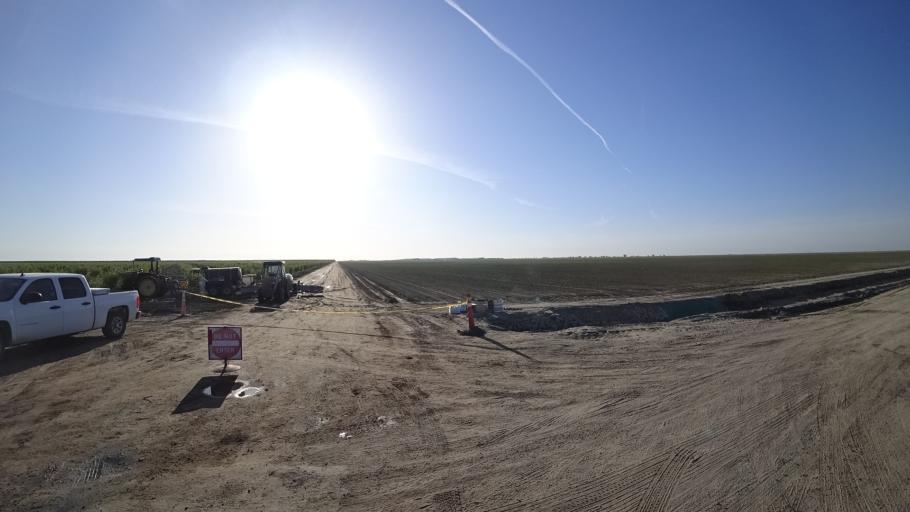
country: US
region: California
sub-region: Kings County
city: Stratford
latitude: 36.1600
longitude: -119.7623
